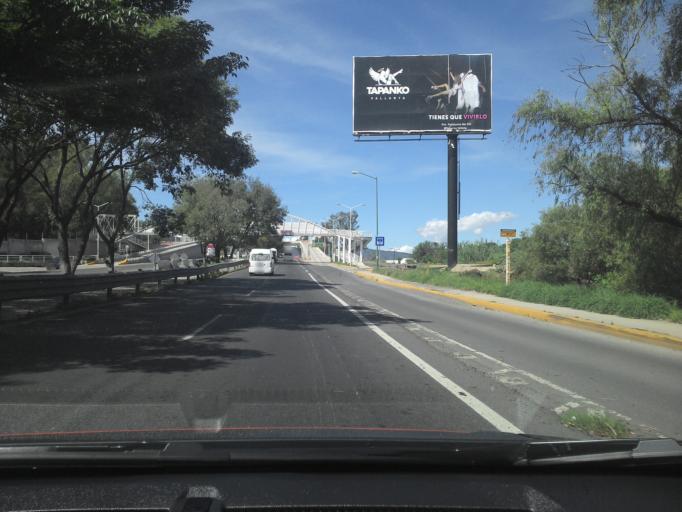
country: MX
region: Jalisco
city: Nuevo Mexico
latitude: 20.7175
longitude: -103.4795
